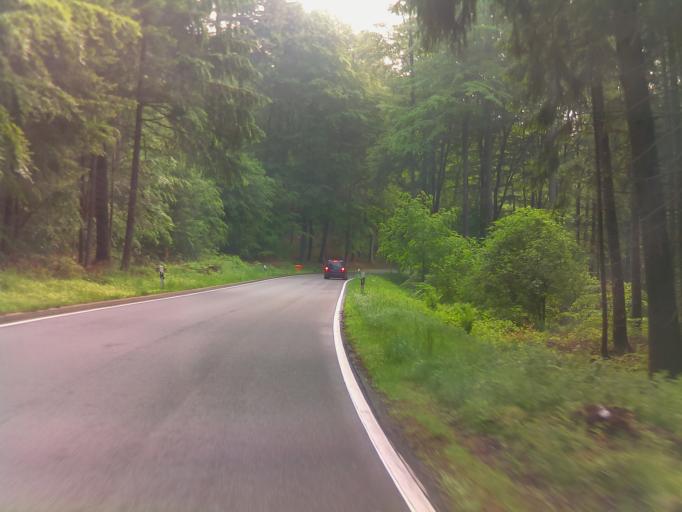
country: DE
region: Bavaria
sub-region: Regierungsbezirk Unterfranken
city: Laudenbach
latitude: 49.7514
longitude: 9.1225
